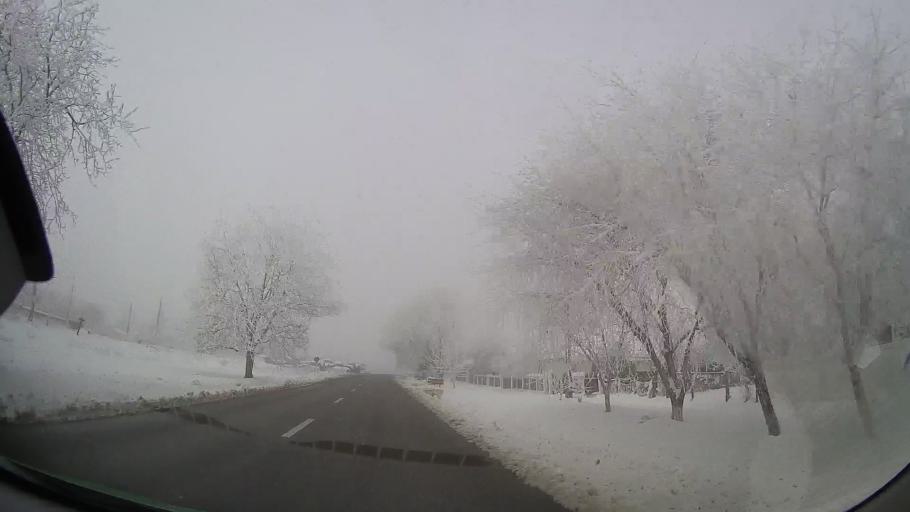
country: RO
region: Iasi
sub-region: Comuna Mircesti
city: Mircesti
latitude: 47.0896
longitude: 26.8233
